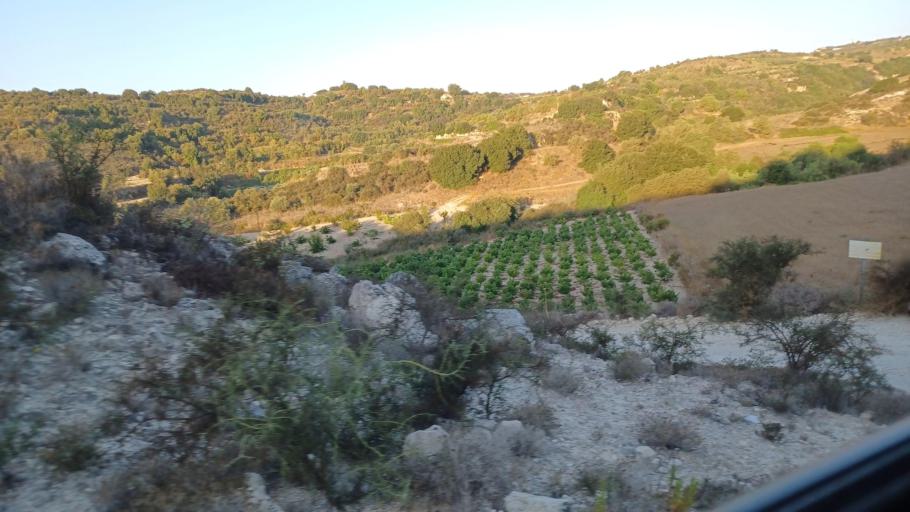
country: CY
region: Pafos
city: Mesogi
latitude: 34.8765
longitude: 32.5276
